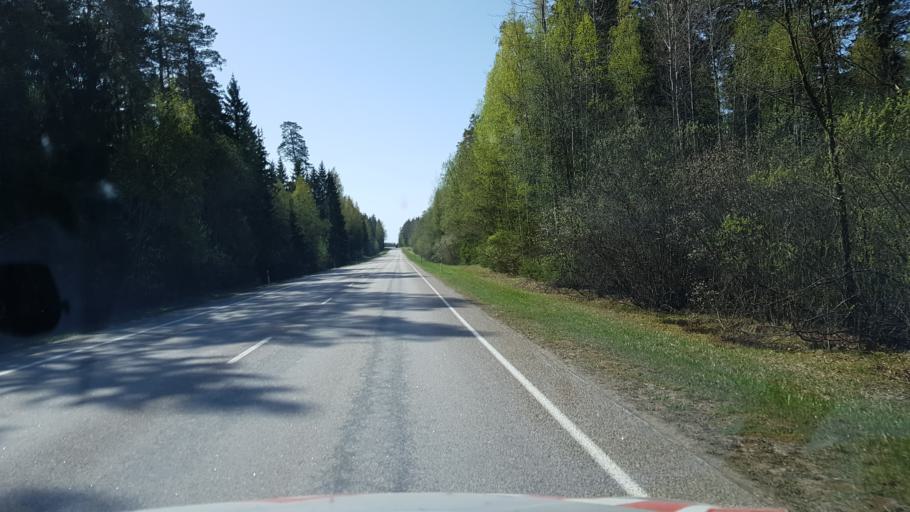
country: EE
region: Valgamaa
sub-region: Valga linn
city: Valga
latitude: 57.8517
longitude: 26.0592
